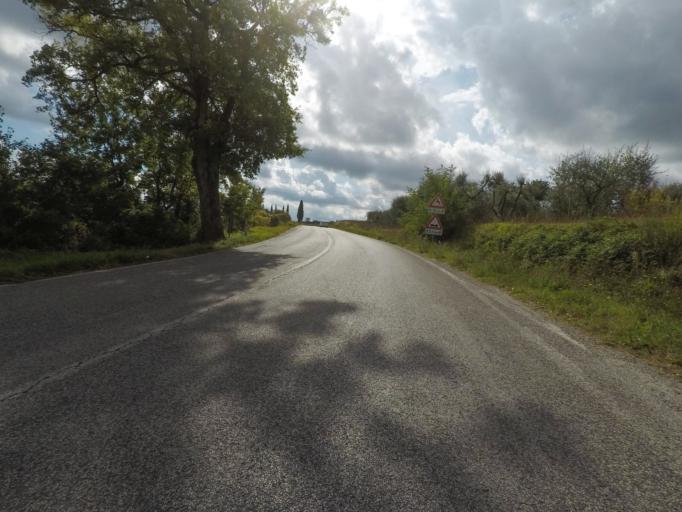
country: IT
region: Tuscany
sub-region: Provincia di Siena
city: Torrita di Siena
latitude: 43.1533
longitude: 11.7772
